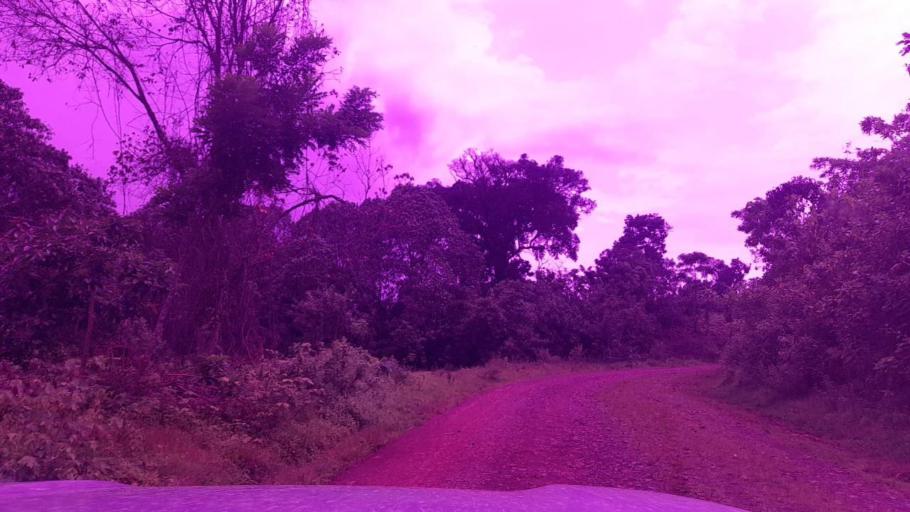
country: ET
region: Southern Nations, Nationalities, and People's Region
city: Tippi
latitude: 7.6305
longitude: 35.5641
